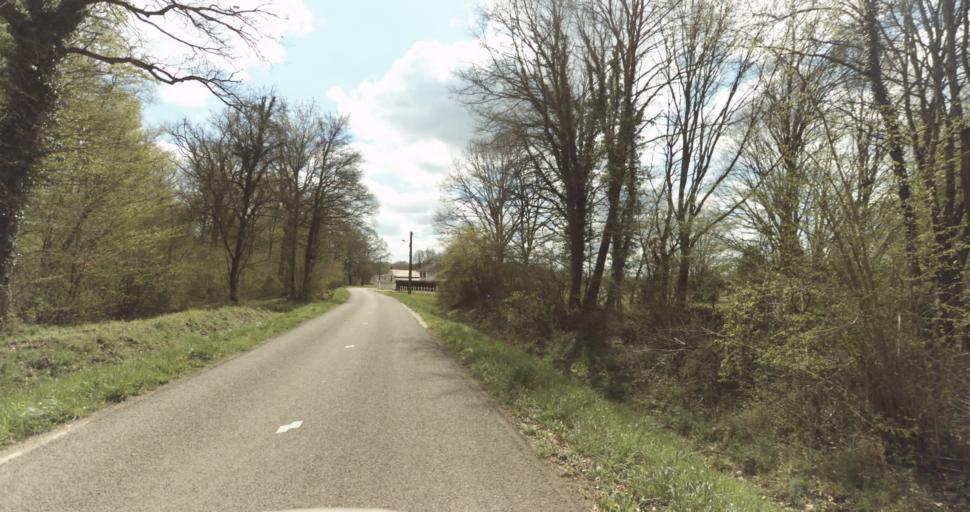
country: FR
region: Bourgogne
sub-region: Departement de la Cote-d'Or
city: Auxonne
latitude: 47.1771
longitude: 5.4222
